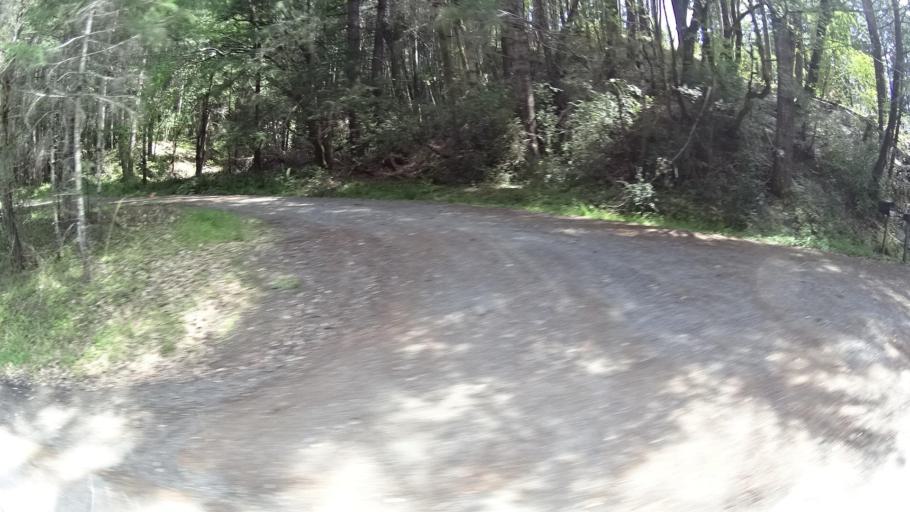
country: US
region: California
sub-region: Humboldt County
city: Redway
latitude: 40.3664
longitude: -123.7297
